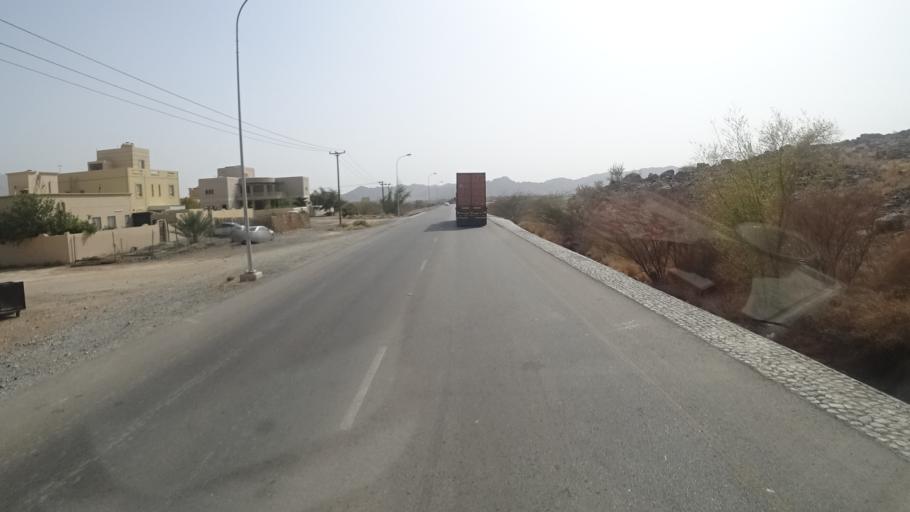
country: OM
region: Muhafazat ad Dakhiliyah
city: Nizwa
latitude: 23.0007
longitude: 57.5518
